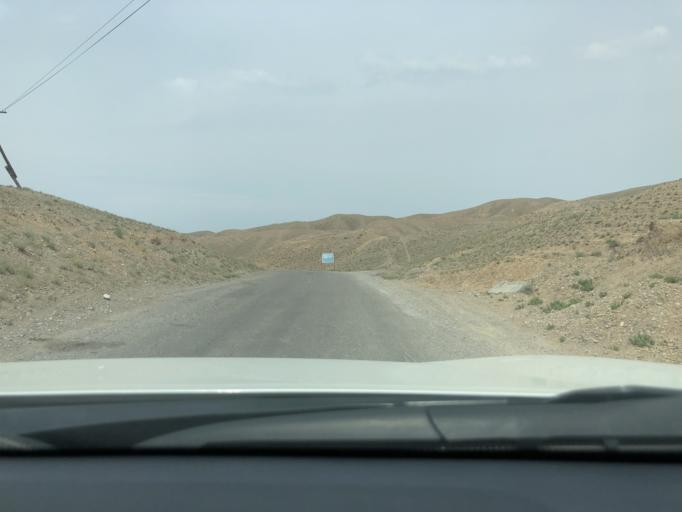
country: TJ
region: Viloyati Sughd
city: Kim
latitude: 40.2171
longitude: 70.4794
